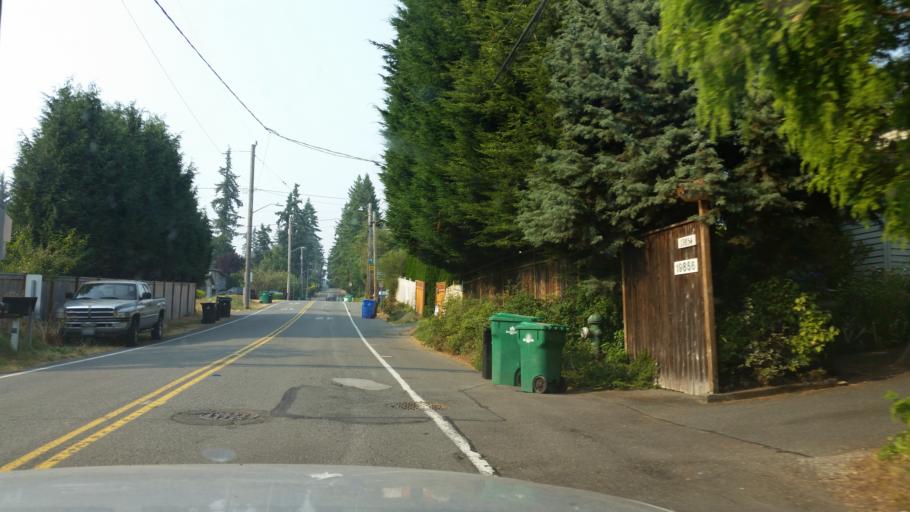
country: US
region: Washington
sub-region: Snohomish County
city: Woodway
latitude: 47.7738
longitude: -122.3773
